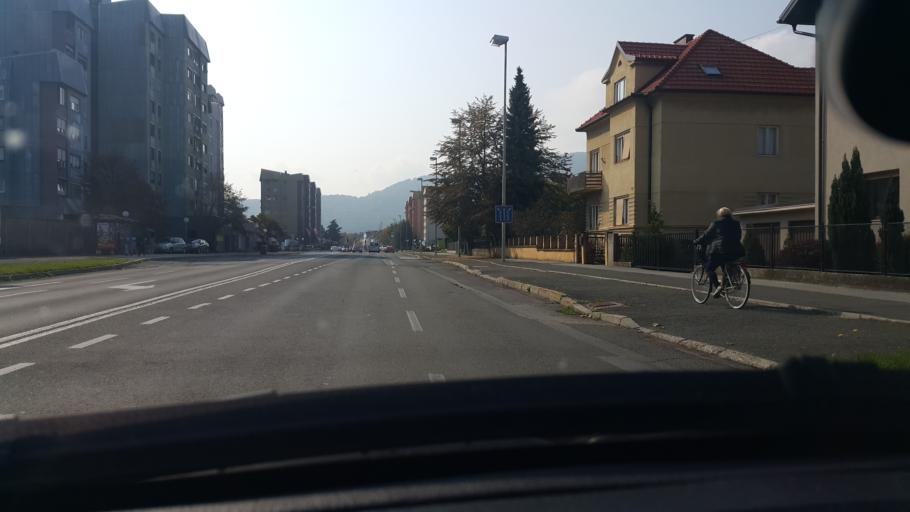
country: SI
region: Maribor
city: Maribor
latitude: 46.5445
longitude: 15.6345
